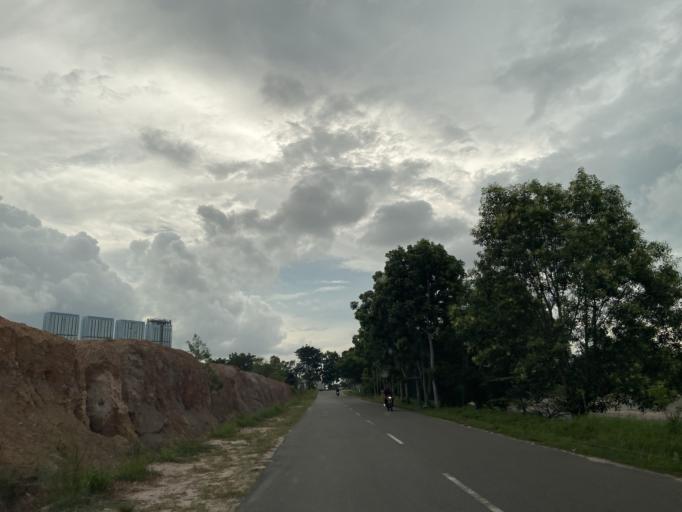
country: SG
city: Singapore
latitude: 1.1239
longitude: 104.0538
